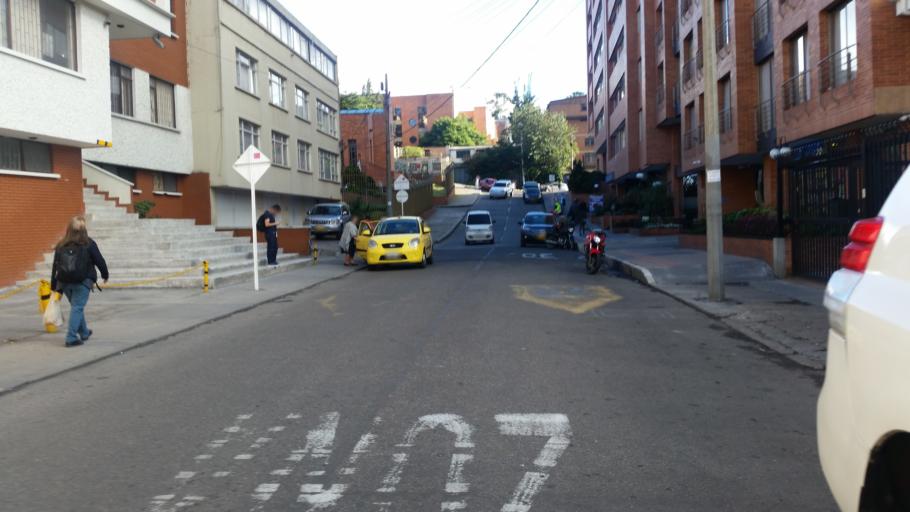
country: CO
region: Bogota D.C.
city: Bogota
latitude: 4.6320
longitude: -74.0632
